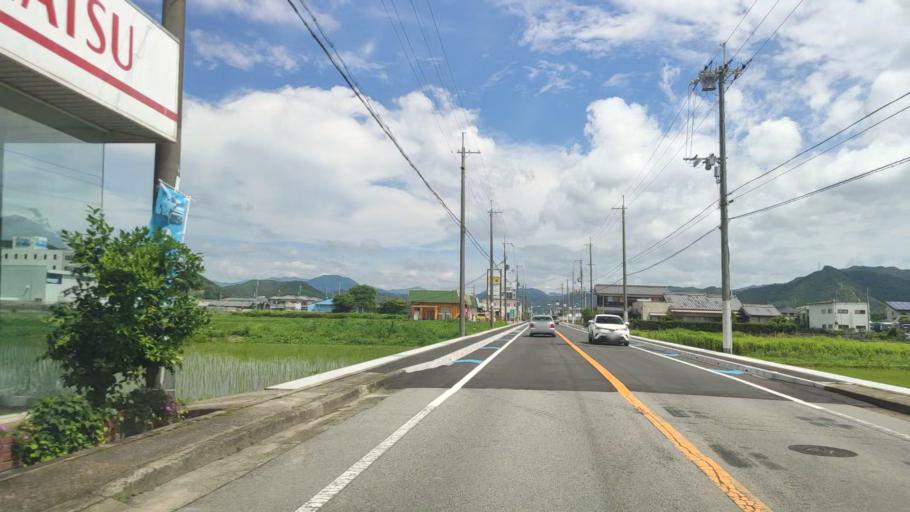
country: JP
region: Hyogo
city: Nishiwaki
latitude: 35.0036
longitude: 134.9625
